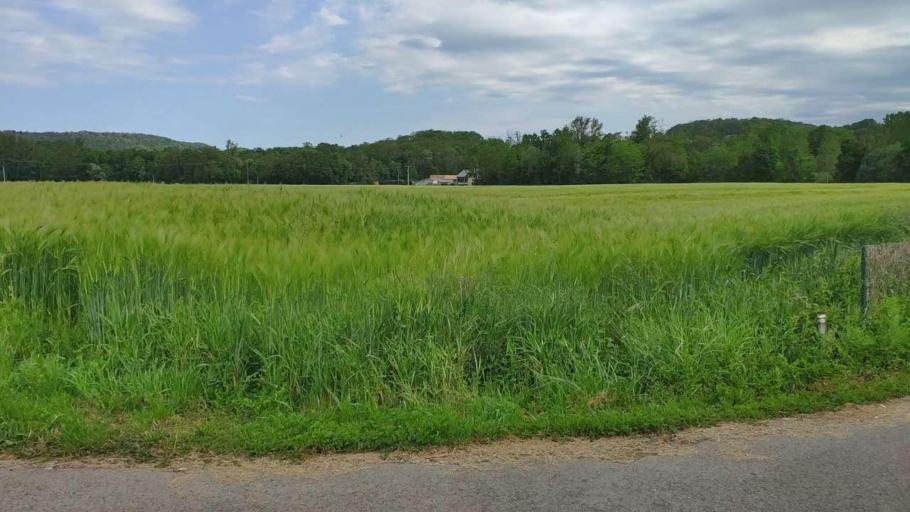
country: FR
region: Franche-Comte
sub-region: Departement du Jura
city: Perrigny
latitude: 46.7683
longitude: 5.5949
